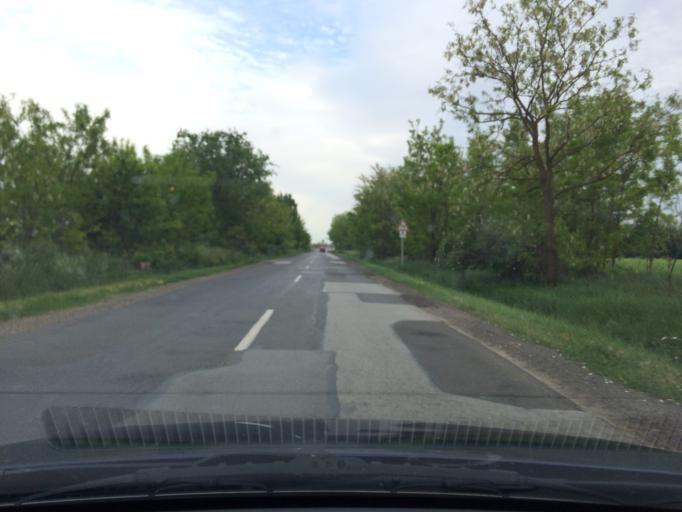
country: HU
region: Hajdu-Bihar
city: Hajdunanas
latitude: 47.8888
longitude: 21.4127
